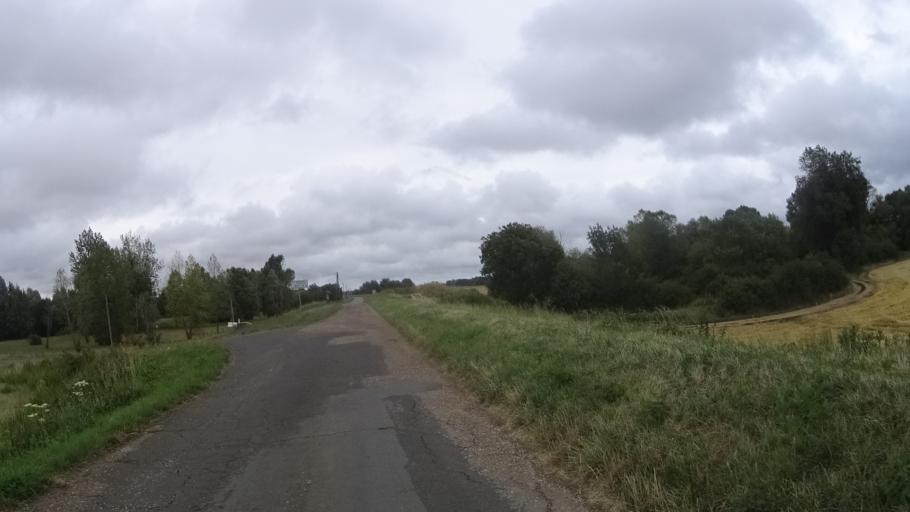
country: FR
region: Centre
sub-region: Departement du Loir-et-Cher
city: Saint-Dye-sur-Loire
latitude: 47.6615
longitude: 1.4834
